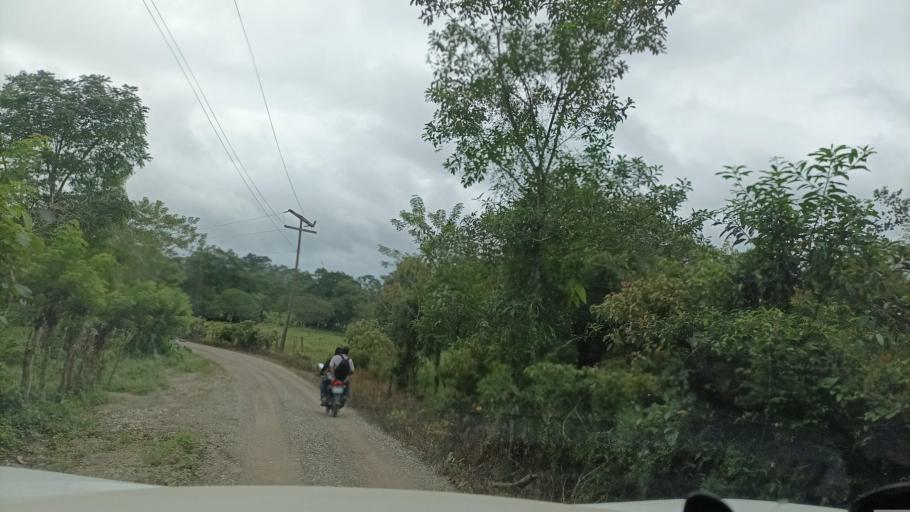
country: MX
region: Veracruz
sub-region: Uxpanapa
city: Poblado 10
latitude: 17.4152
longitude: -94.4182
